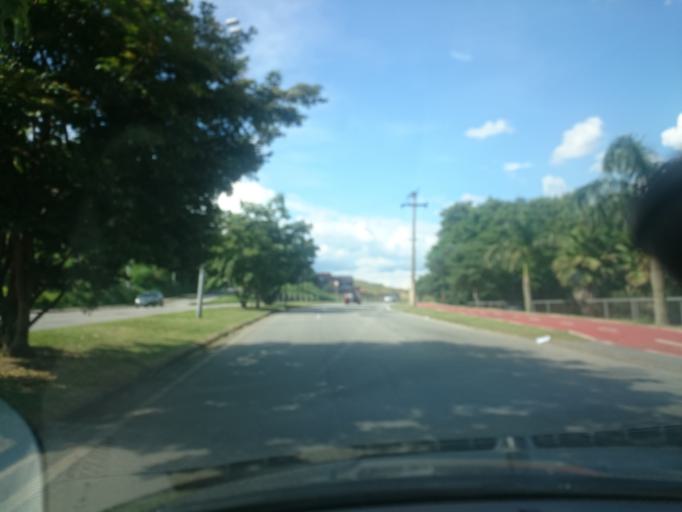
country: BR
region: Sao Paulo
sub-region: Sorocaba
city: Sorocaba
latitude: -23.5196
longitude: -47.4531
